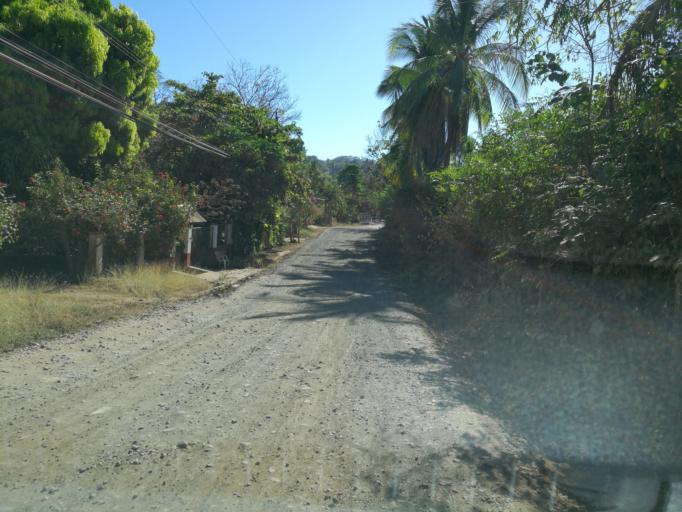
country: CR
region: Puntarenas
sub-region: Canton Central de Puntarenas
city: Puntarenas
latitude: 10.0953
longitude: -84.9805
